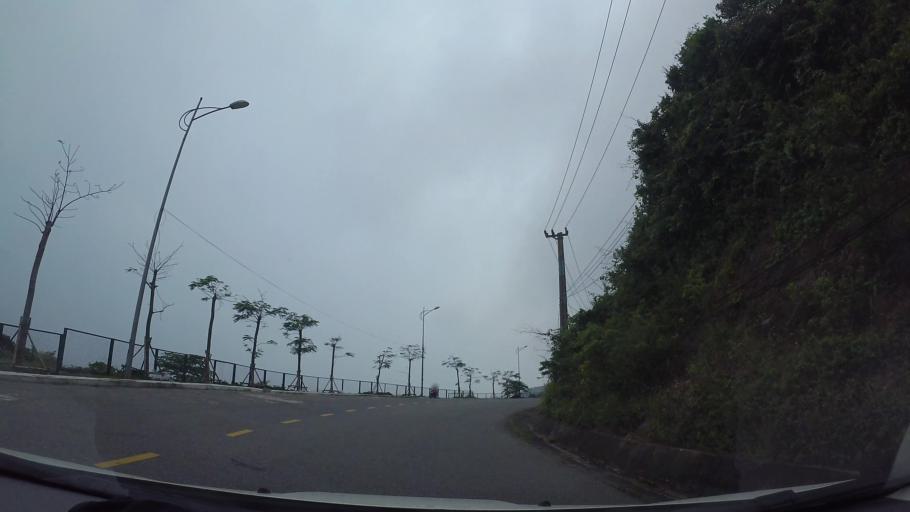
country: VN
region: Da Nang
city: Son Tra
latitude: 16.1153
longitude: 108.3109
